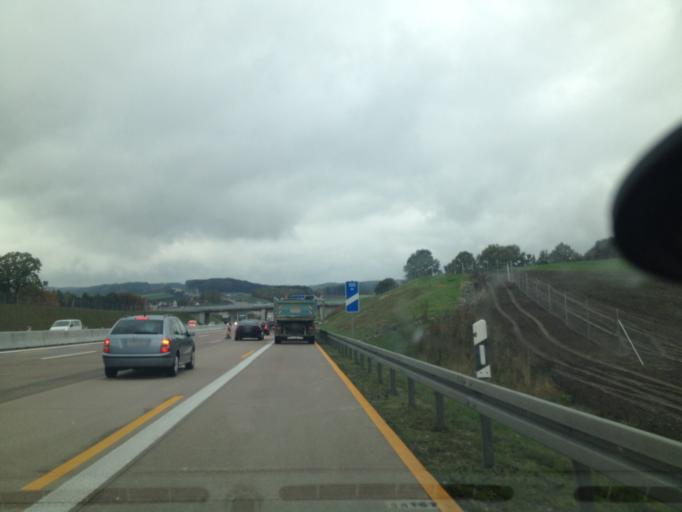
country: DE
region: Bavaria
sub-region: Swabia
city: Zusmarshausen
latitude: 48.4100
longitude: 10.6031
